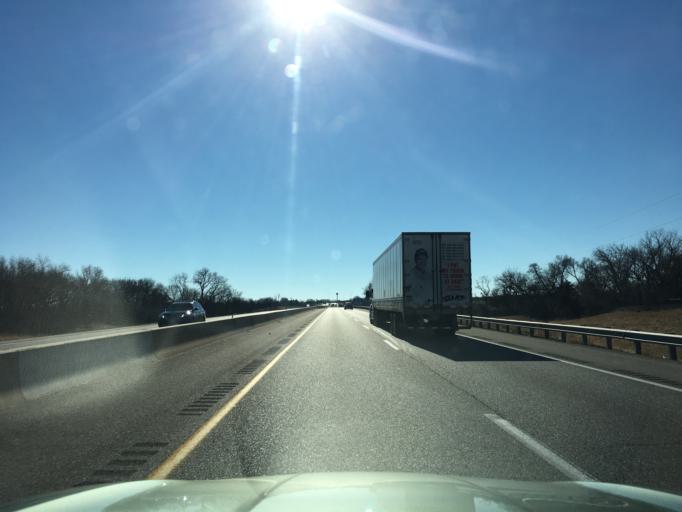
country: US
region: Kansas
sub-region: Sumner County
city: Belle Plaine
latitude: 37.3850
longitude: -97.3246
